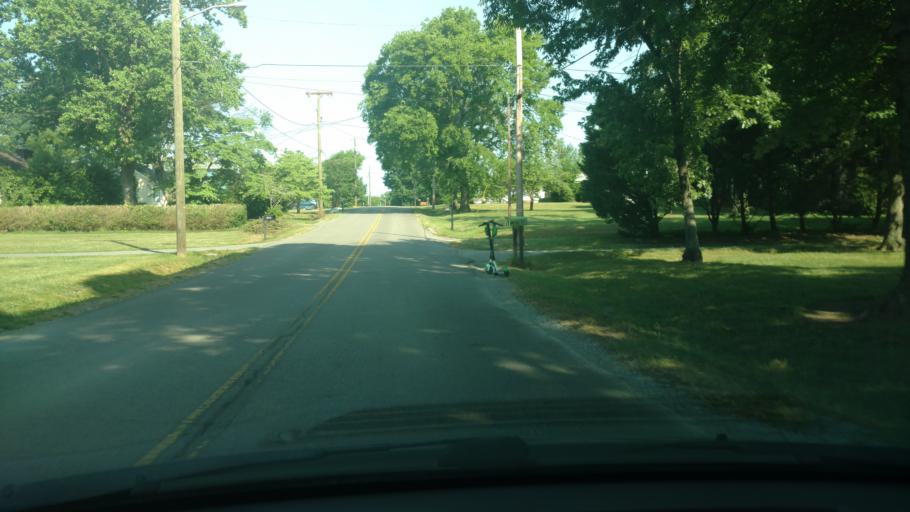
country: US
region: Tennessee
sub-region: Davidson County
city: Nashville
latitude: 36.2200
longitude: -86.7187
